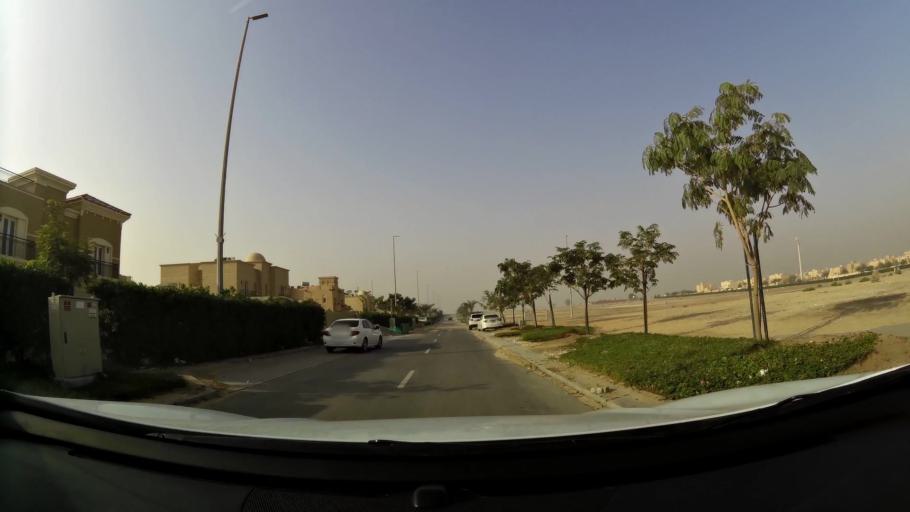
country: AE
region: Abu Dhabi
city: Abu Dhabi
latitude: 24.3006
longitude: 54.6179
